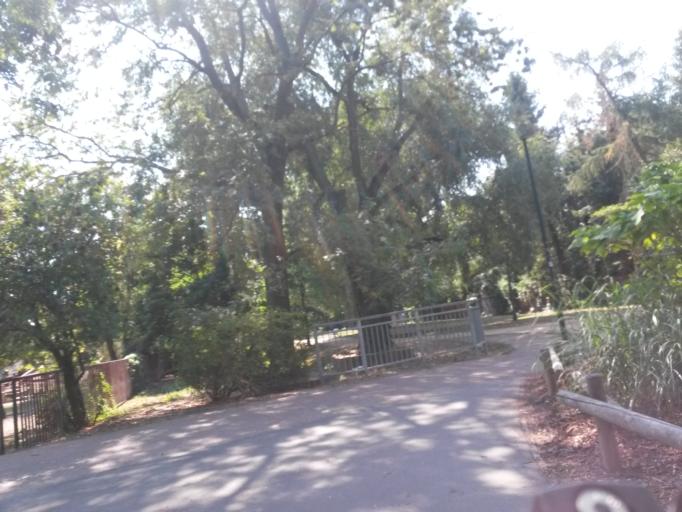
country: DE
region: Saxony-Anhalt
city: Wittenburg
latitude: 51.8745
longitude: 12.6590
